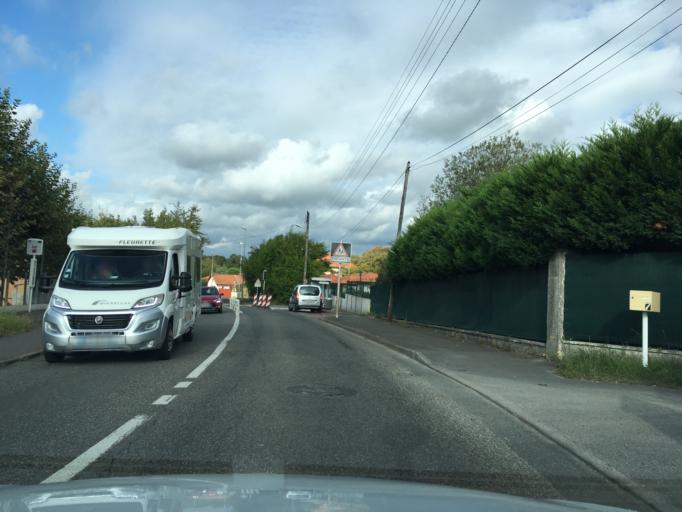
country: FR
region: Aquitaine
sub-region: Departement des Pyrenees-Atlantiques
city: Anglet
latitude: 43.4584
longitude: -1.4983
